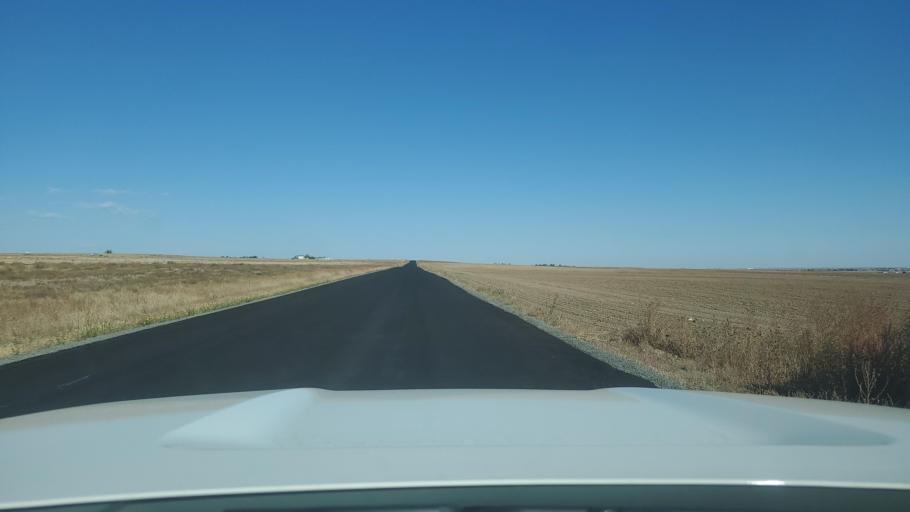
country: US
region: Colorado
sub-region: Adams County
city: Bennett
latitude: 39.7460
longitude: -104.3772
